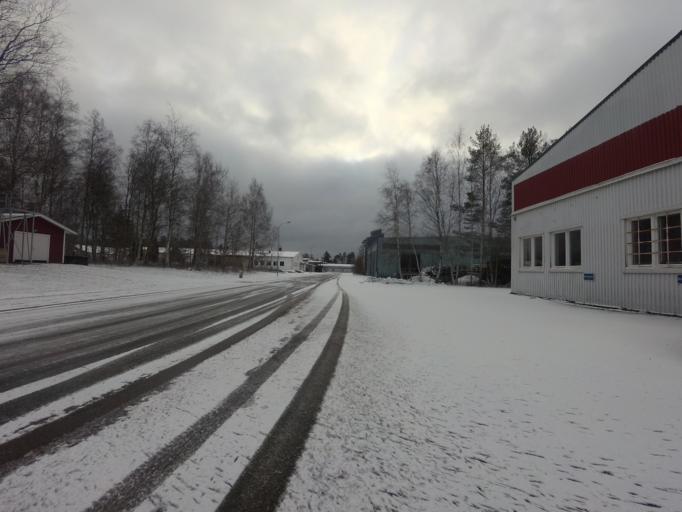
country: SE
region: Skane
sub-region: Osby Kommun
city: Lonsboda
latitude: 56.3953
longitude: 14.3090
